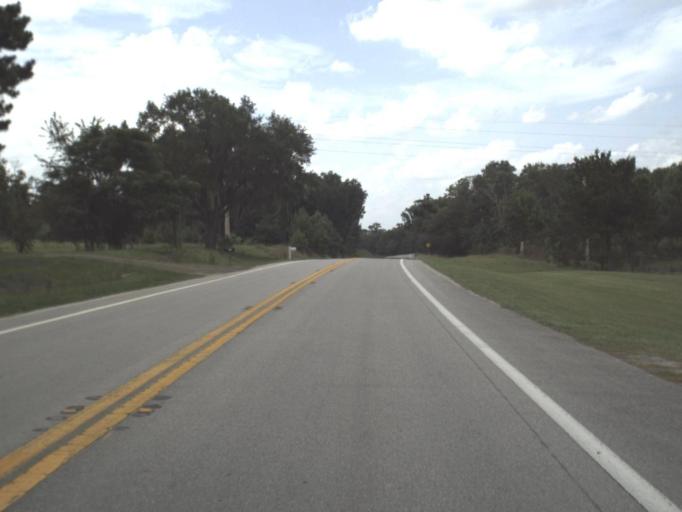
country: US
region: Florida
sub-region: Madison County
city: Madison
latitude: 30.5247
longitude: -83.4226
